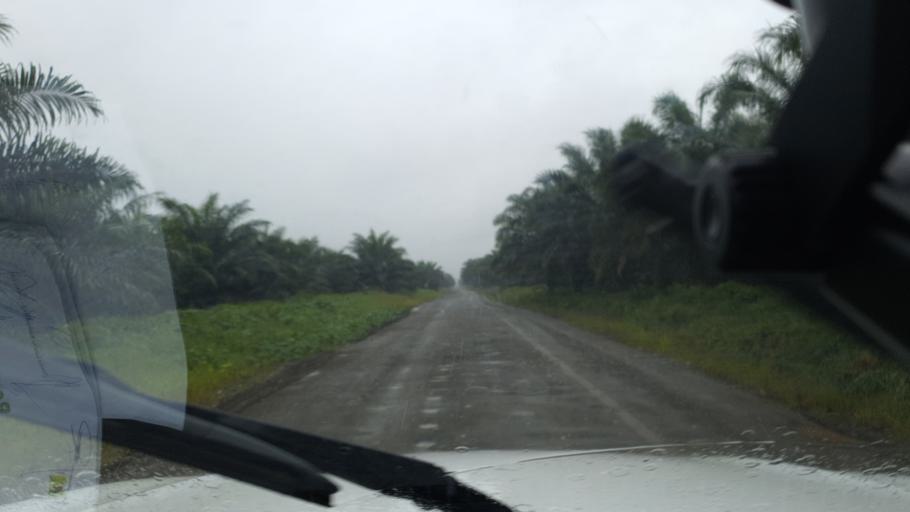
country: SB
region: Guadalcanal
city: Honiara
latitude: -9.4701
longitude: 160.1562
